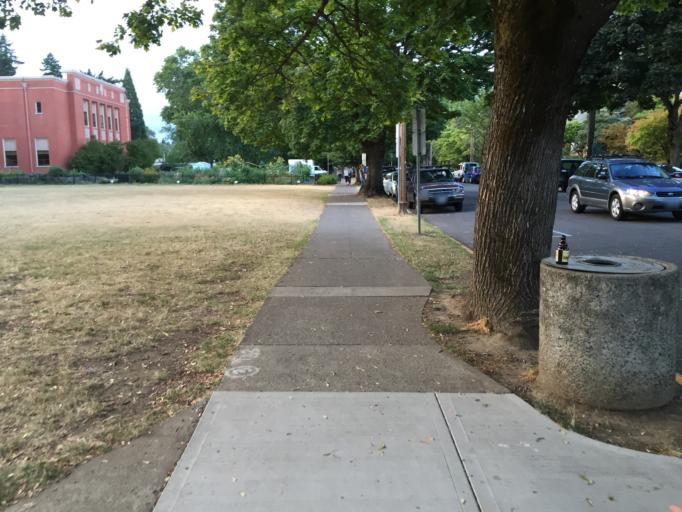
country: US
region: Oregon
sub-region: Multnomah County
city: Portland
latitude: 45.5391
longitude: -122.6262
